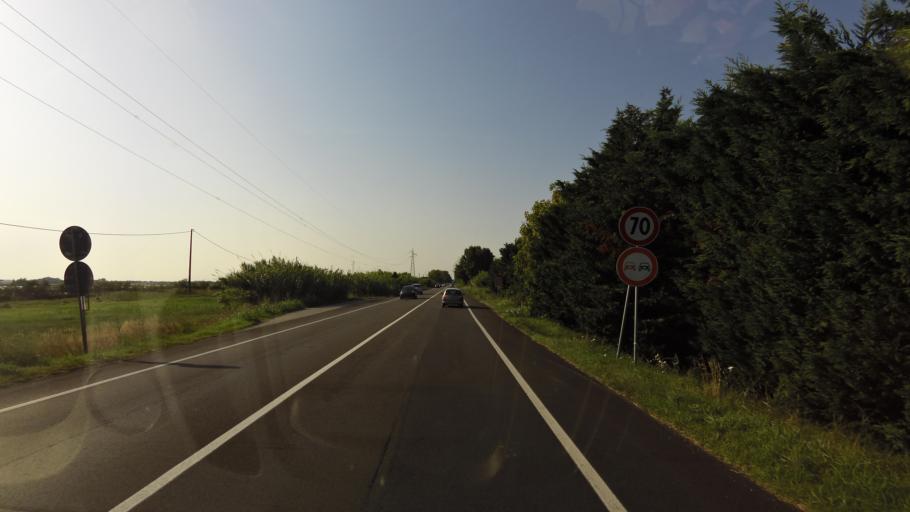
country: IT
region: Emilia-Romagna
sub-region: Provincia di Ravenna
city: Cervia
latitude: 44.2405
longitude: 12.3540
